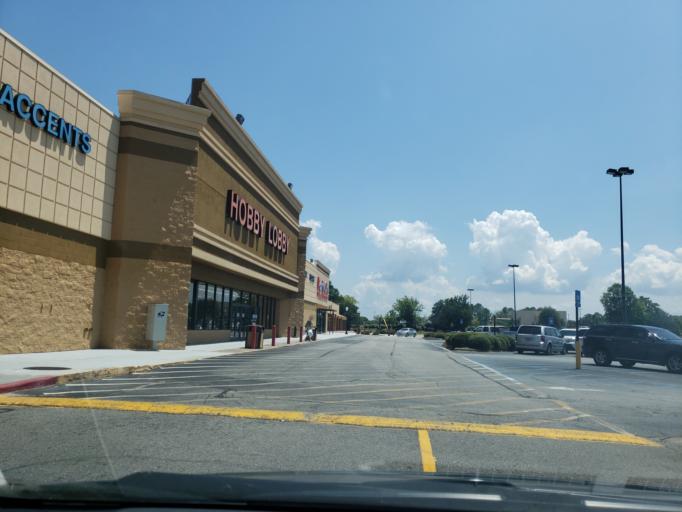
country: US
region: Georgia
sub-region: Dougherty County
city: Albany
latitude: 31.6207
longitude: -84.2231
